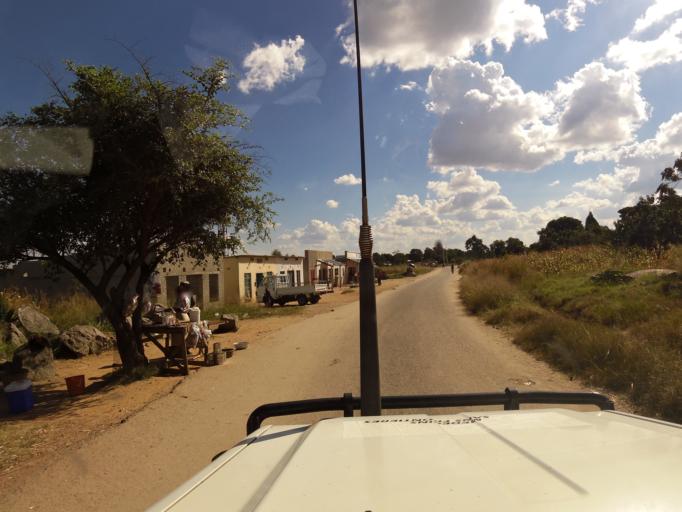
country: ZW
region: Harare
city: Epworth
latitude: -17.8745
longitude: 31.1438
